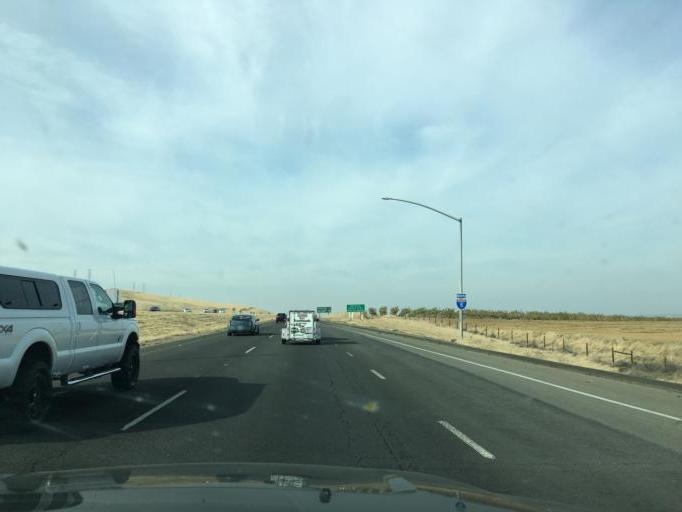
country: US
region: California
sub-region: Merced County
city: Los Banos
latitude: 36.9319
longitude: -120.8421
